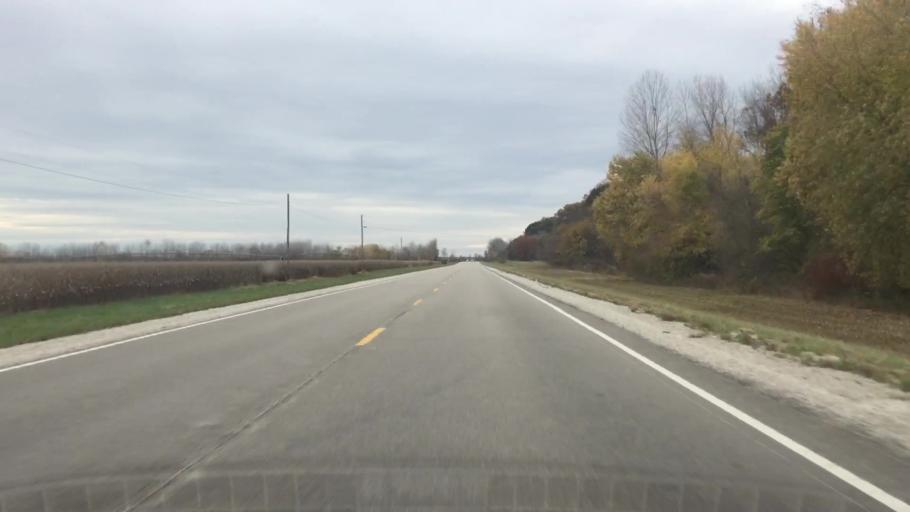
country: US
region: Missouri
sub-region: Callaway County
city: Holts Summit
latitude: 38.5811
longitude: -92.1016
